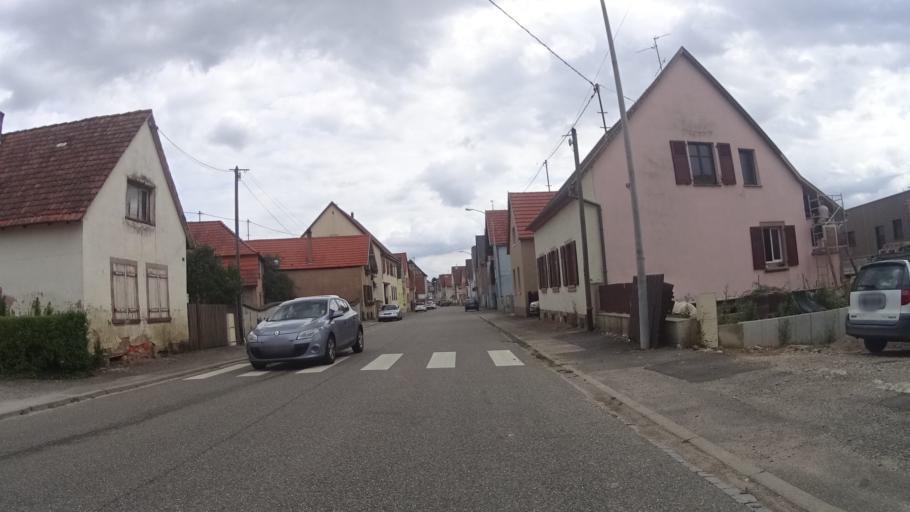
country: FR
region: Alsace
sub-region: Departement du Bas-Rhin
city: Geudertheim
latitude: 48.7230
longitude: 7.7450
